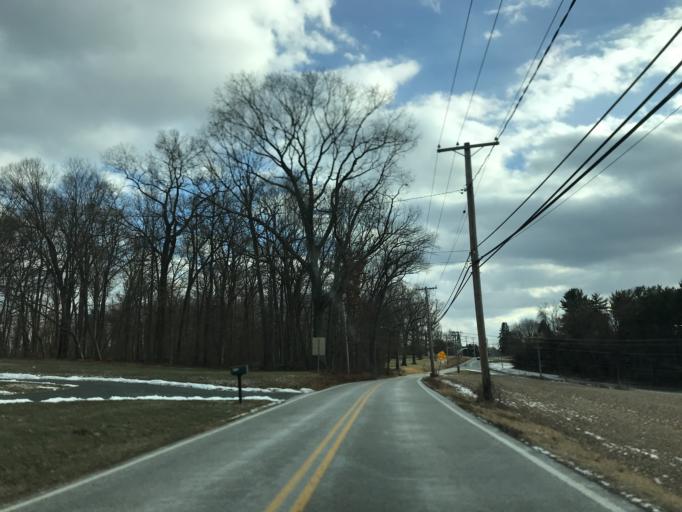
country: US
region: Maryland
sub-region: Harford County
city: Jarrettsville
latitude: 39.6064
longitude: -76.4421
